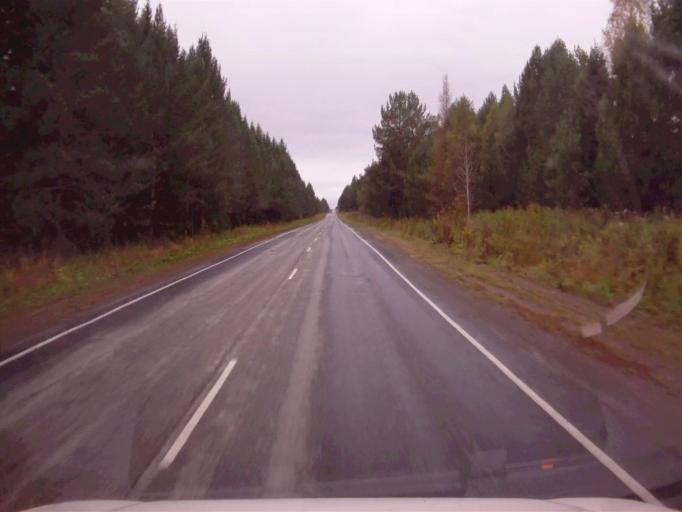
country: RU
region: Chelyabinsk
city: Nyazepetrovsk
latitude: 56.0673
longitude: 59.6919
